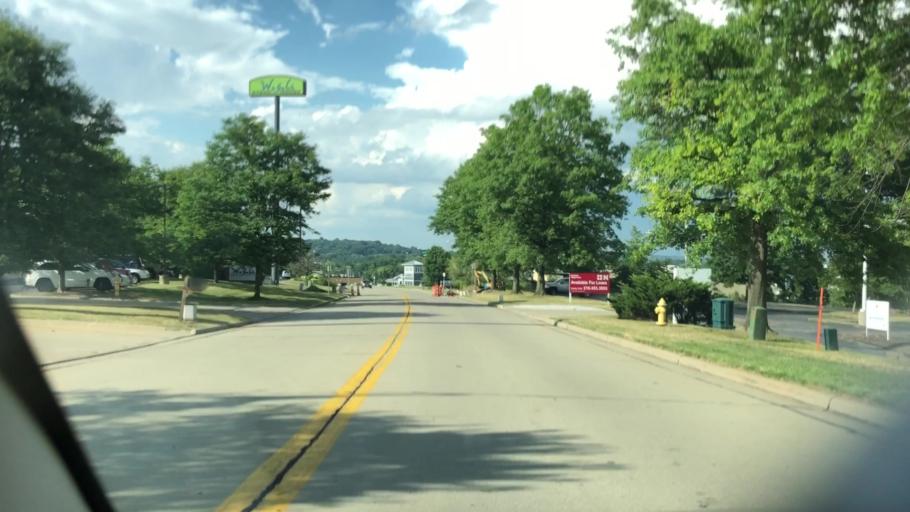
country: US
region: Ohio
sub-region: Summit County
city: Montrose-Ghent
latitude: 41.1298
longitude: -81.6538
